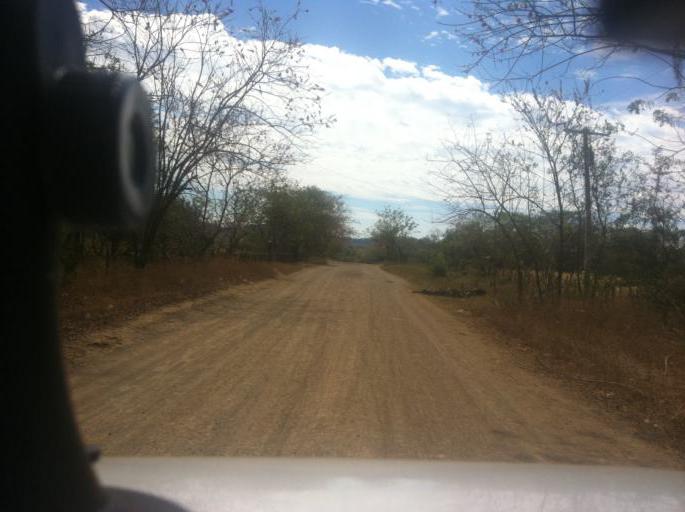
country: NI
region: Granada
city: Nandaime
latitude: 11.6270
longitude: -86.0229
